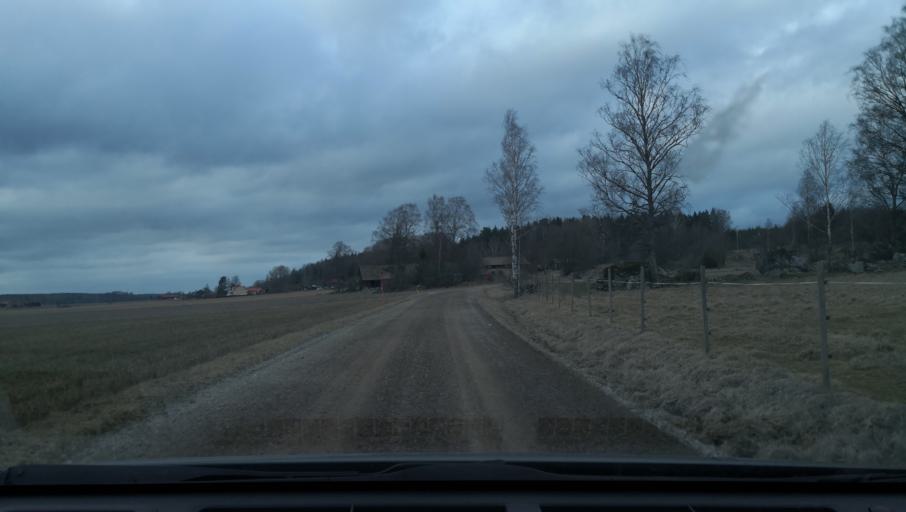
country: SE
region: Vaestmanland
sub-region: Kopings Kommun
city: Koping
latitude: 59.5249
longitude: 15.9091
